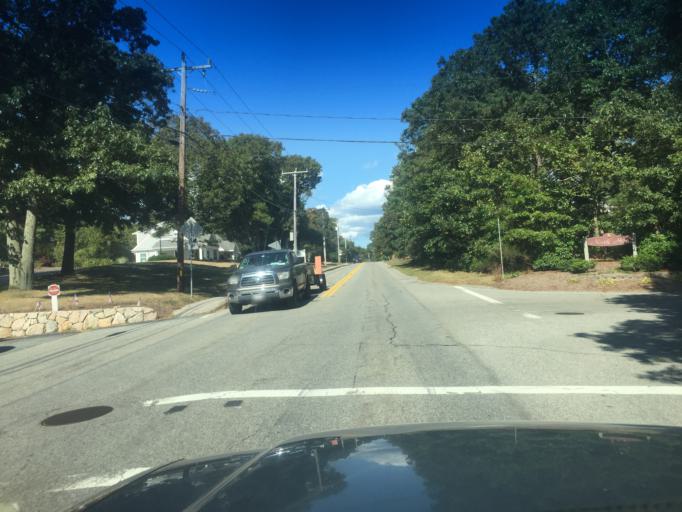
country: US
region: Massachusetts
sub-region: Barnstable County
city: North Falmouth
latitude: 41.6511
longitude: -70.6122
